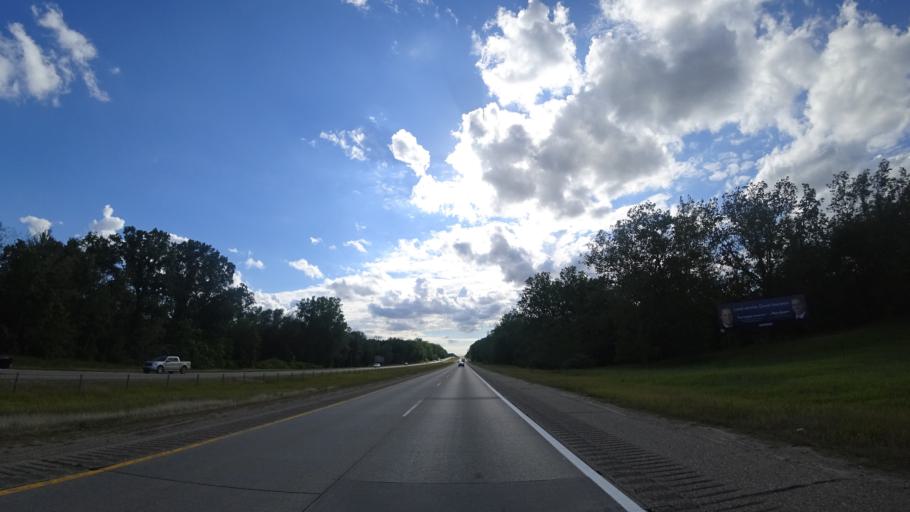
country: US
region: Michigan
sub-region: Kent County
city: Lowell
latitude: 42.8788
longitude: -85.3922
